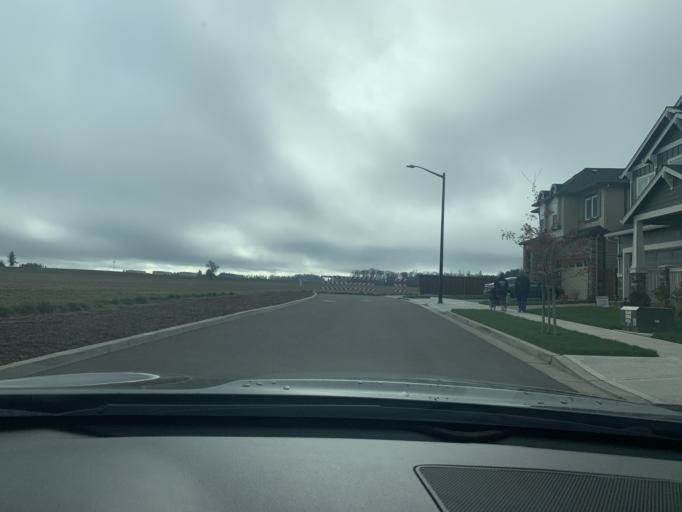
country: US
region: Oregon
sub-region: Washington County
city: North Plains
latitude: 45.5930
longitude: -122.9743
